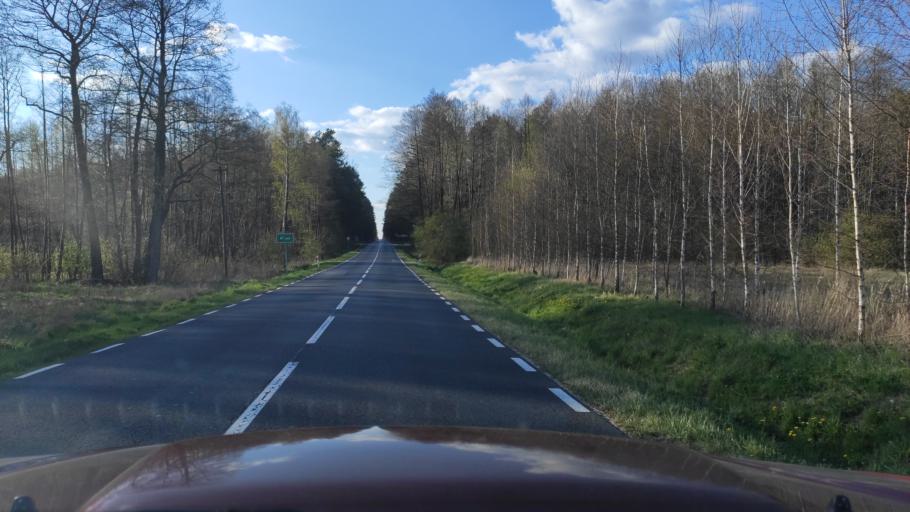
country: PL
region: Masovian Voivodeship
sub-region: Powiat zwolenski
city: Zwolen
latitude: 51.3860
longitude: 21.5544
